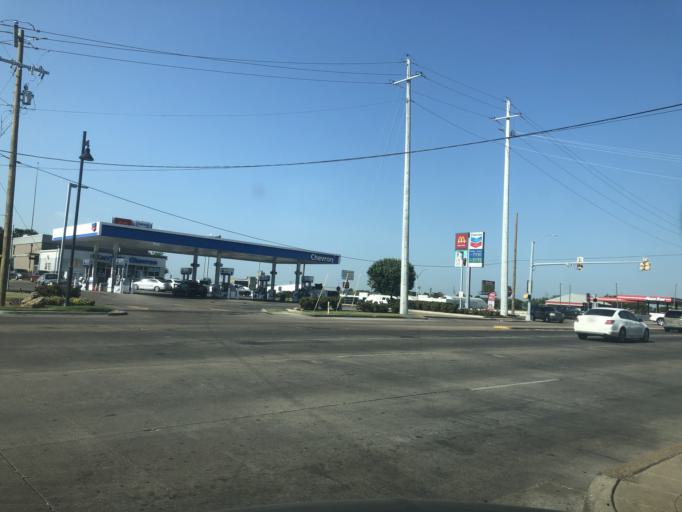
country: US
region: Texas
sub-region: Tarrant County
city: Fort Worth
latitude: 32.7061
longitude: -97.3195
